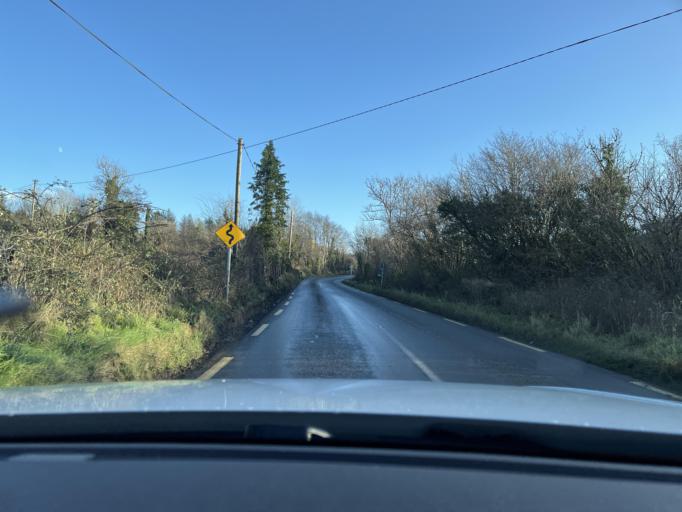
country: IE
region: Connaught
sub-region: County Leitrim
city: Manorhamilton
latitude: 54.2411
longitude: -8.2225
